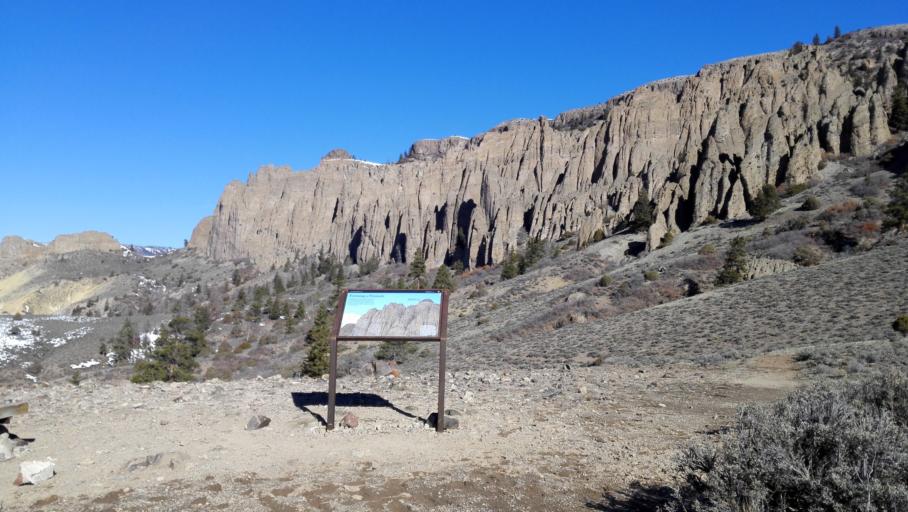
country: US
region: Colorado
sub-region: Gunnison County
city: Gunnison
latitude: 38.4805
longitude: -107.2629
